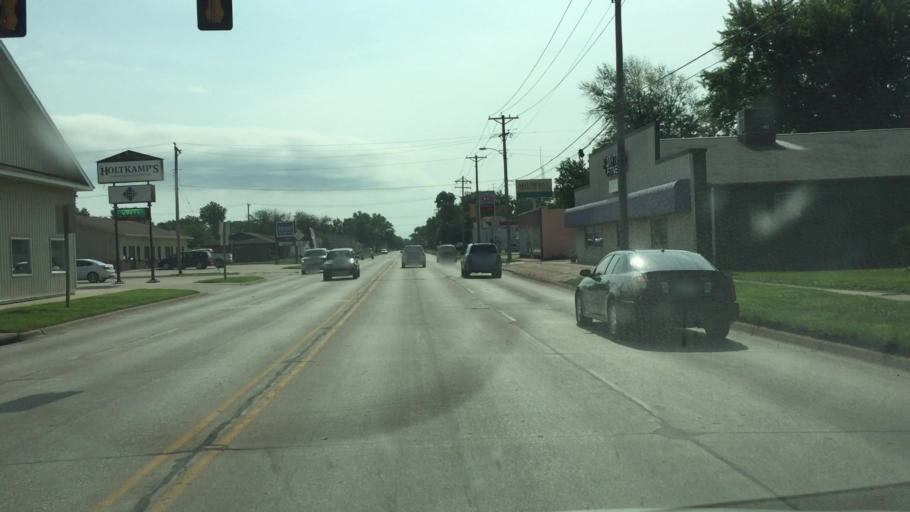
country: US
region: Iowa
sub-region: Lee County
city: Fort Madison
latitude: 40.6271
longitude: -91.3396
